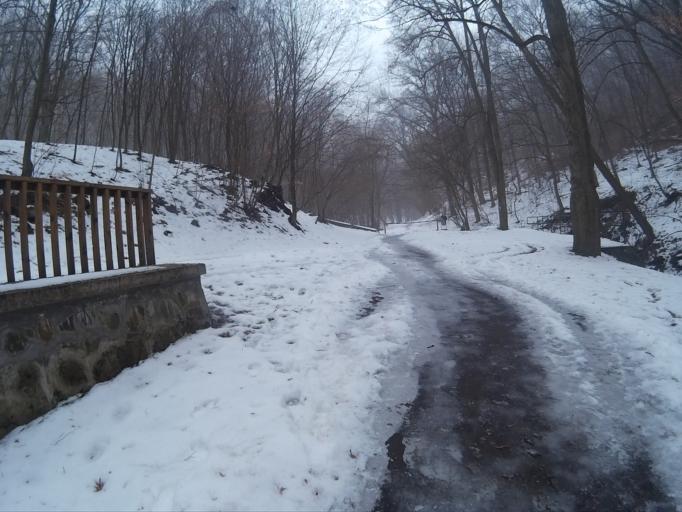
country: HU
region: Nograd
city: Matraverebely
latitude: 48.0007
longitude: 19.7600
